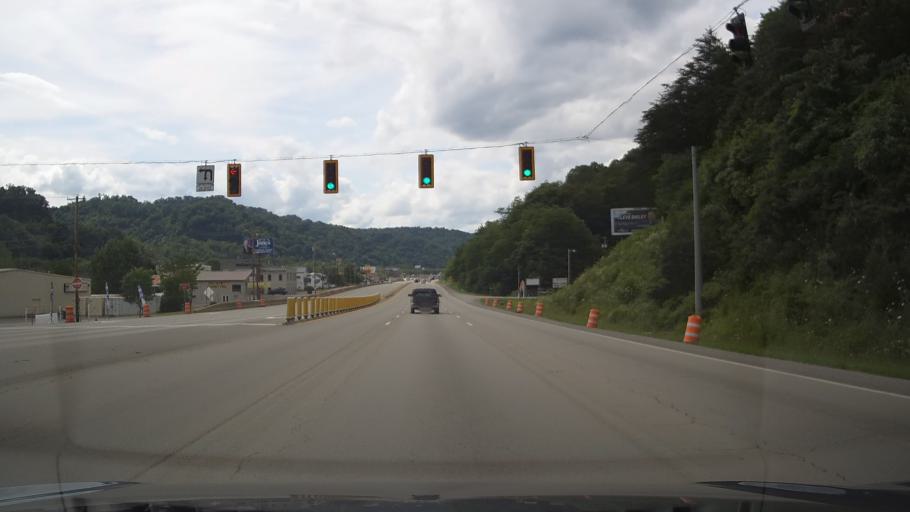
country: US
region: Kentucky
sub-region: Pike County
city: Coal Run Village
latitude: 37.5152
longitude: -82.5591
